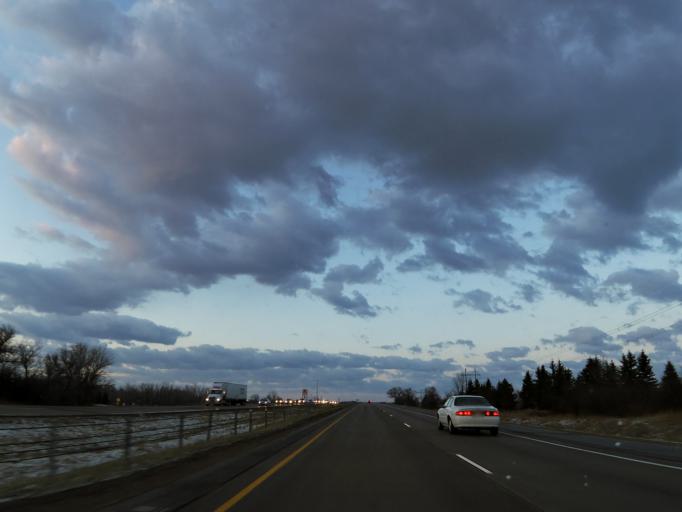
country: US
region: Minnesota
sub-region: Dakota County
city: Lakeville
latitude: 44.6561
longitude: -93.2943
